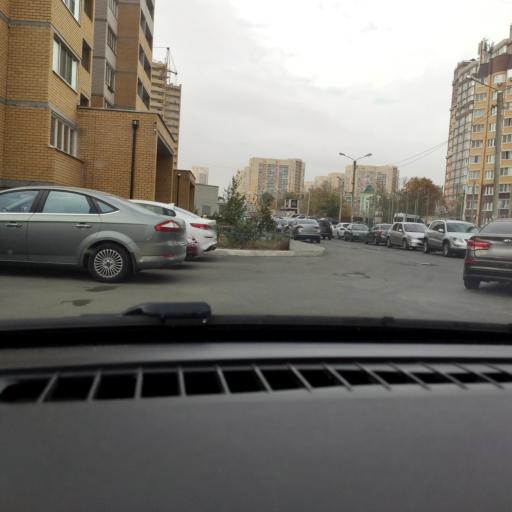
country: RU
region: Voronezj
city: Voronezh
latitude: 51.7024
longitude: 39.2079
